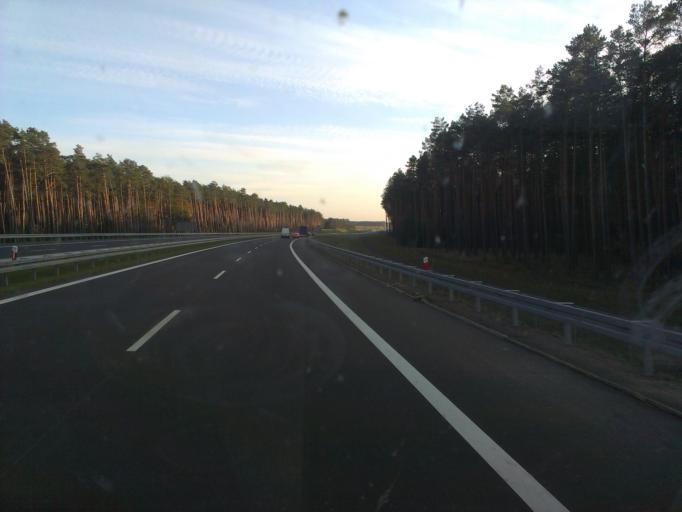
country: PL
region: Lubusz
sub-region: Powiat miedzyrzecki
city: Skwierzyna
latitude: 52.5530
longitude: 15.5382
